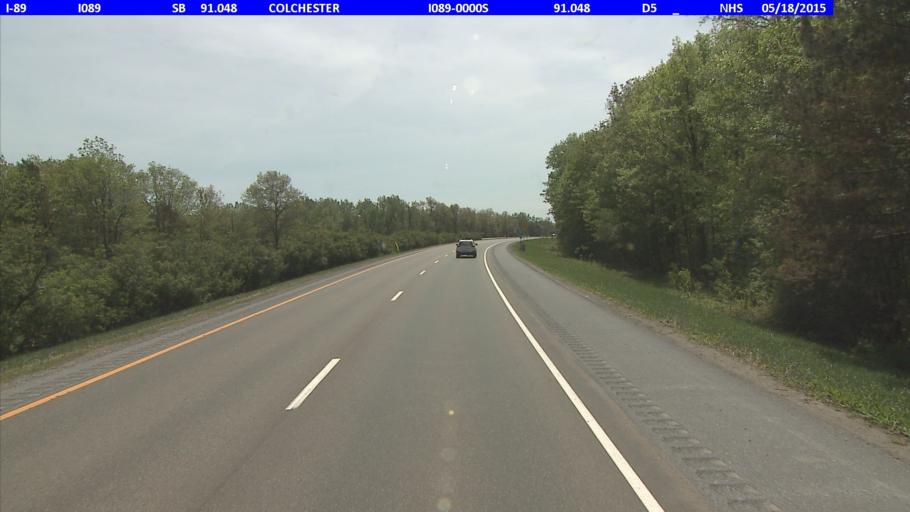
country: US
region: Vermont
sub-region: Chittenden County
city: Winooski
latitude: 44.5014
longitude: -73.1749
